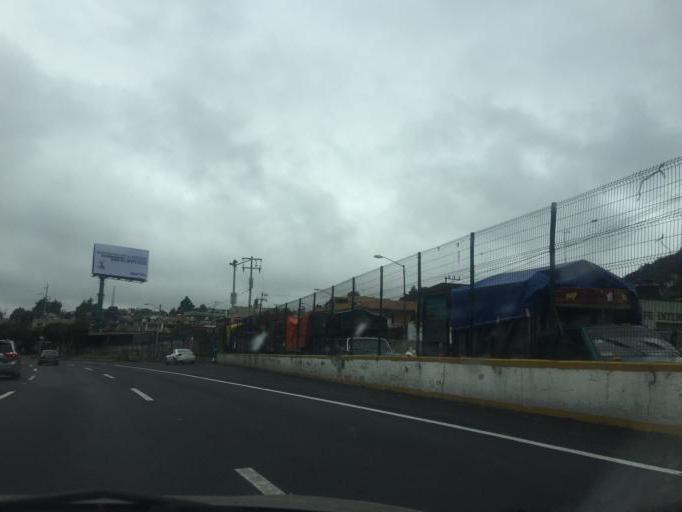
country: MX
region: Mexico City
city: Xochimilco
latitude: 19.2000
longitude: -99.1428
